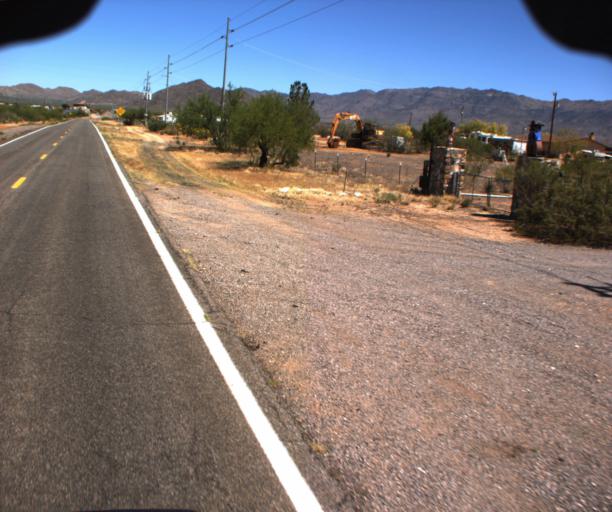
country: US
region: Arizona
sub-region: Yavapai County
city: Congress
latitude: 34.1491
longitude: -112.8430
